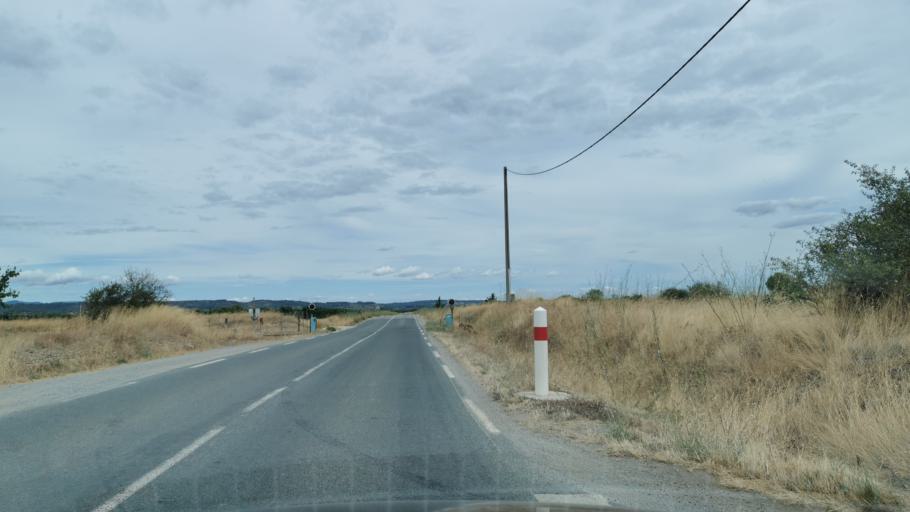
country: FR
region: Languedoc-Roussillon
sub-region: Departement de l'Aude
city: Argeliers
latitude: 43.2905
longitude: 2.9008
